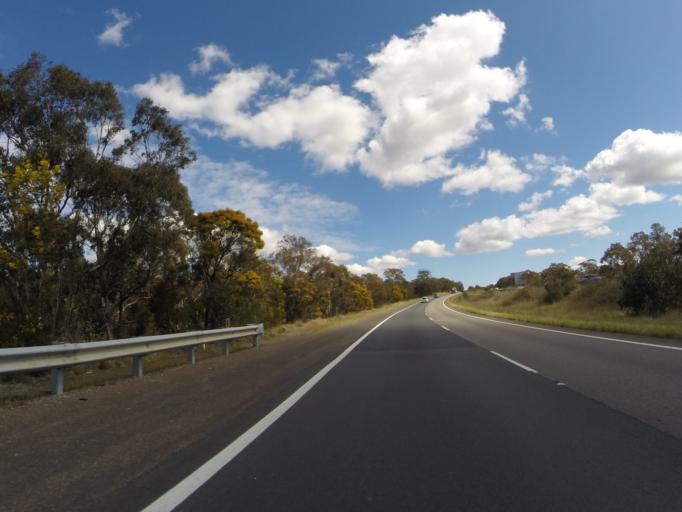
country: AU
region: New South Wales
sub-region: Goulburn Mulwaree
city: Goulburn
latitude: -34.7346
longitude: 149.9688
